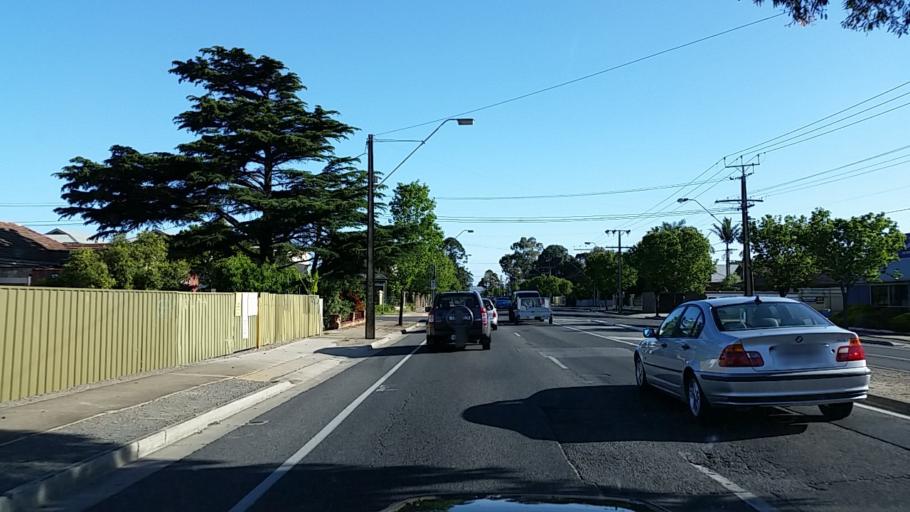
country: AU
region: South Australia
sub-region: City of West Torrens
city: Plympton
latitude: -34.9527
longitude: 138.5540
